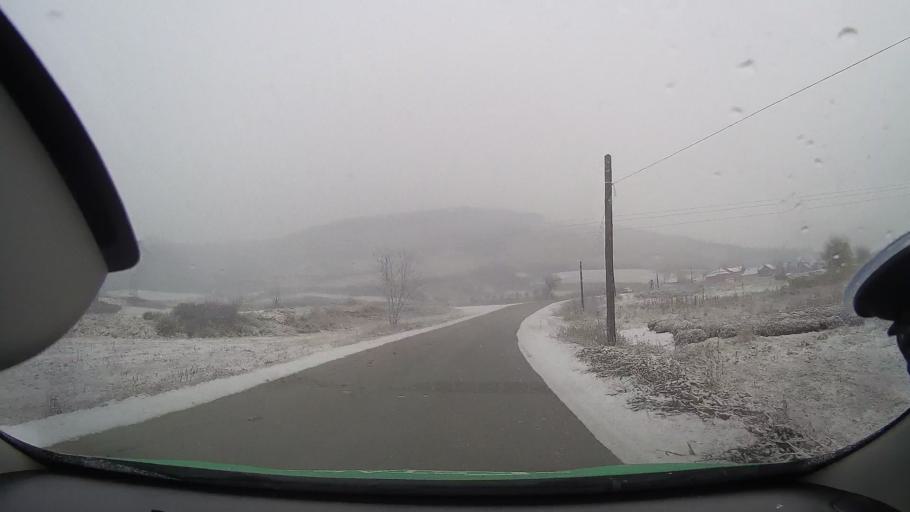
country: RO
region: Alba
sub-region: Municipiul Aiud
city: Ciumbrud
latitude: 46.3131
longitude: 23.7810
